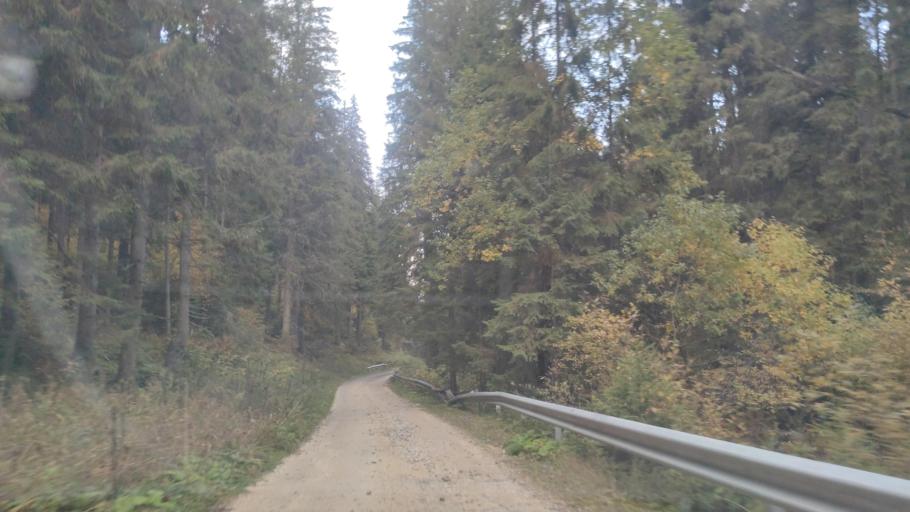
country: RO
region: Harghita
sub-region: Comuna Madaras
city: Madaras
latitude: 46.4740
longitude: 25.6466
